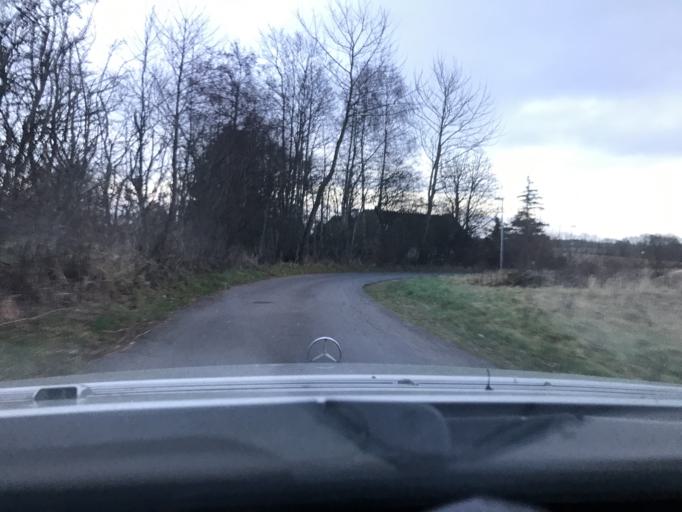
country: DK
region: South Denmark
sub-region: Sonderborg Kommune
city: Nordborg
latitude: 55.0545
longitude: 9.7066
